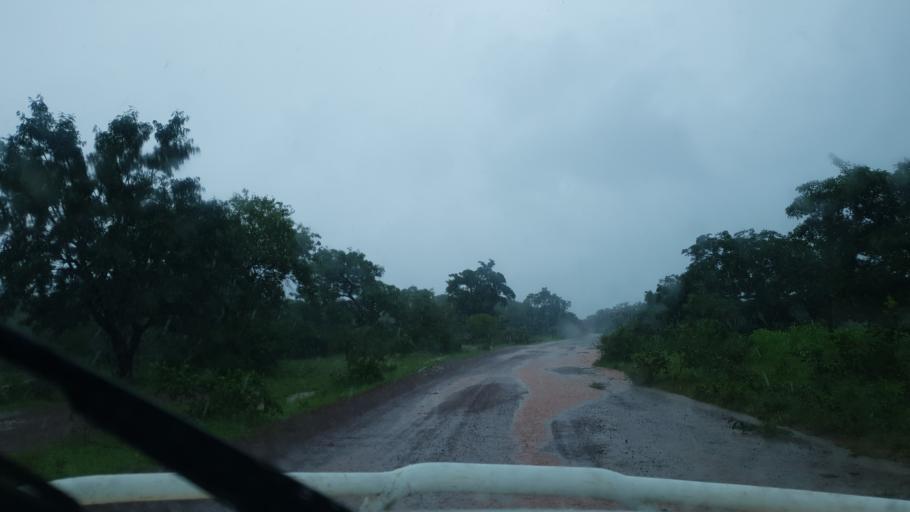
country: ML
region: Sikasso
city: Kolondieba
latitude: 11.6130
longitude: -6.6761
